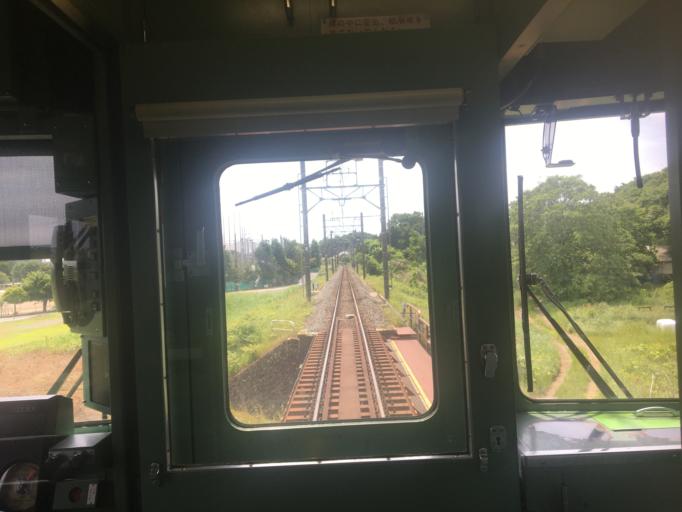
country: JP
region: Saitama
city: Sakado
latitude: 35.9351
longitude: 139.3498
